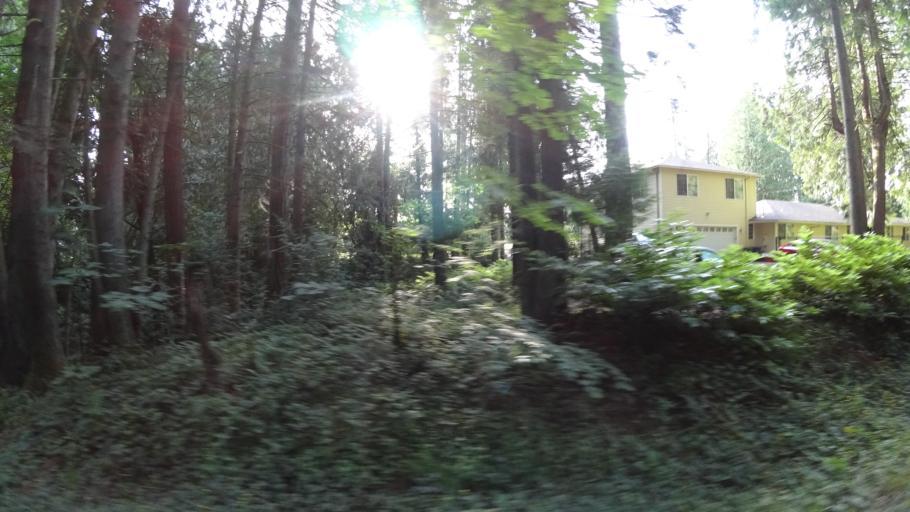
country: US
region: Oregon
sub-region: Clackamas County
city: Happy Valley
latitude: 45.4597
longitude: -122.4968
